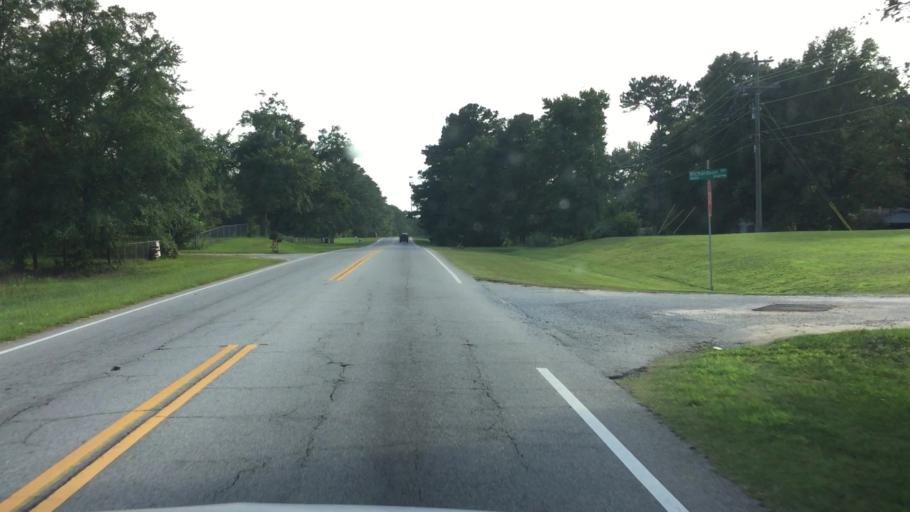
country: US
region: Georgia
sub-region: DeKalb County
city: Pine Mountain
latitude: 33.5907
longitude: -84.1397
